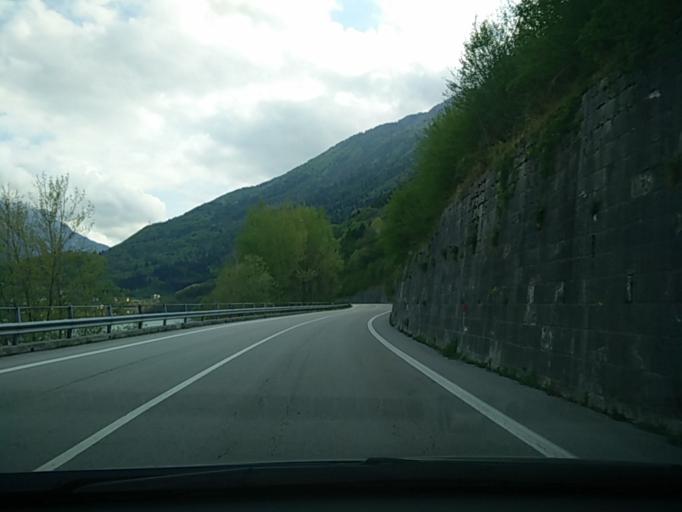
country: IT
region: Veneto
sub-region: Provincia di Belluno
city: Farra d'Alpago
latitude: 46.1046
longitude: 12.3277
